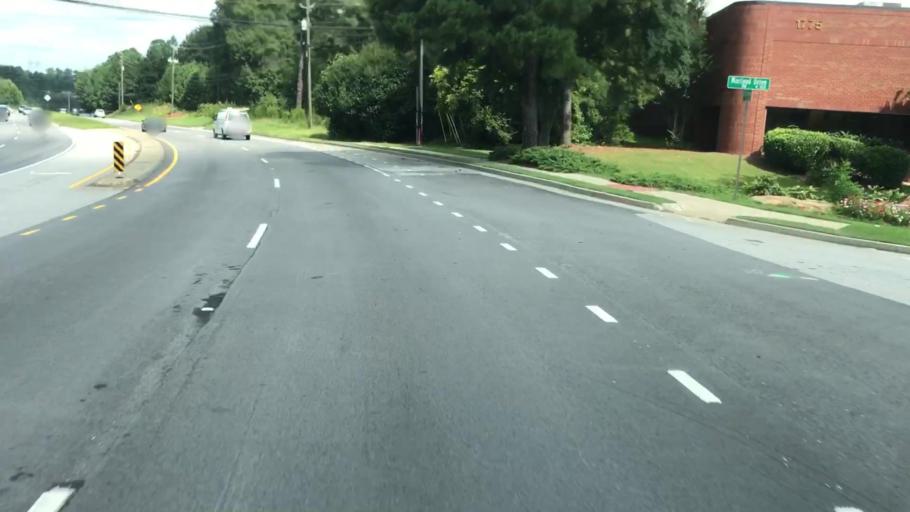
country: US
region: Georgia
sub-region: Gwinnett County
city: Lawrenceville
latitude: 33.9640
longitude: -84.0628
